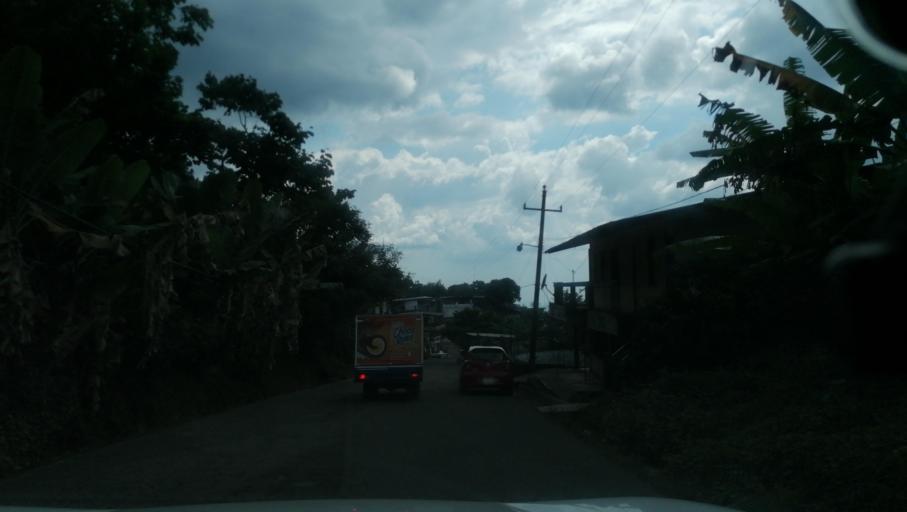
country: MX
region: Chiapas
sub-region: Cacahoatan
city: Benito Juarez
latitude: 15.0787
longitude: -92.1979
